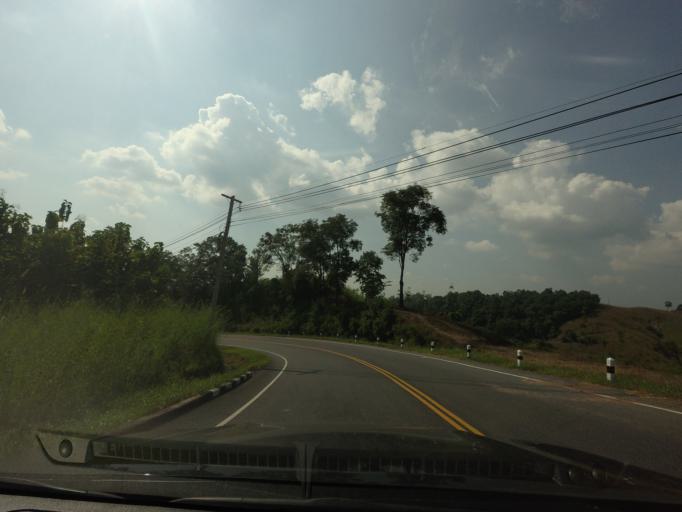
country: TH
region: Nan
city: Santi Suk
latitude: 18.9829
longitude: 100.9500
